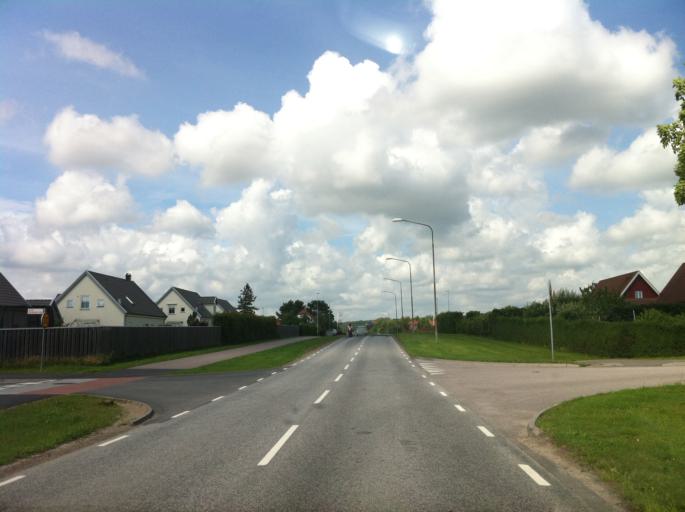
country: SE
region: Skane
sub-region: Trelleborgs Kommun
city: Anderslov
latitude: 55.4928
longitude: 13.3804
